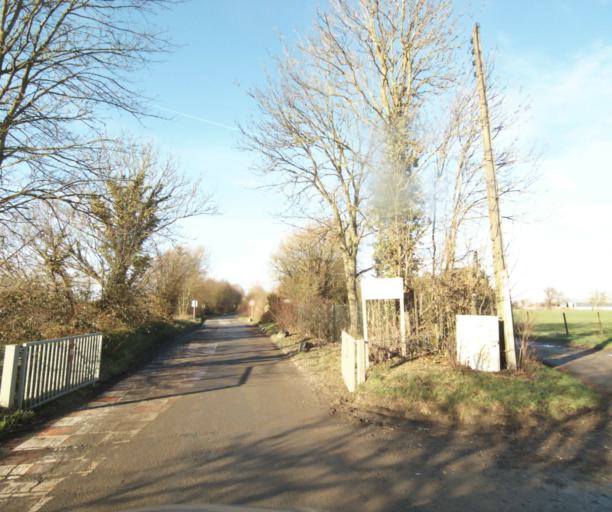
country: FR
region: Nord-Pas-de-Calais
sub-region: Departement du Nord
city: Curgies
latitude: 50.3219
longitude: 3.6015
